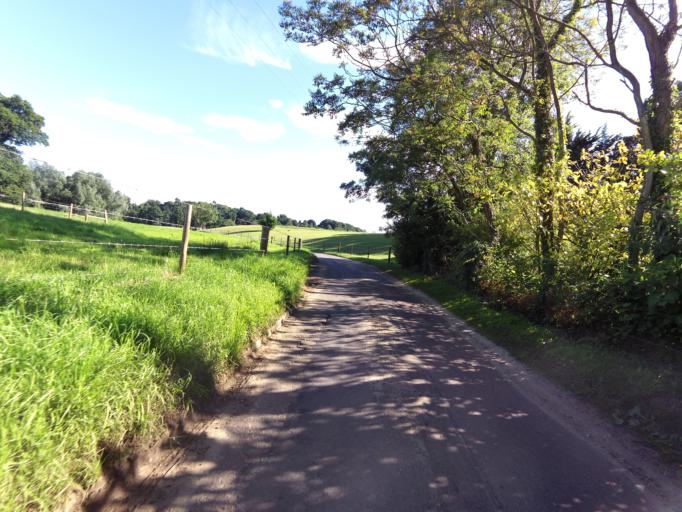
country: GB
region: England
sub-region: Suffolk
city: Kesgrave
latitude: 52.0460
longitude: 1.2518
